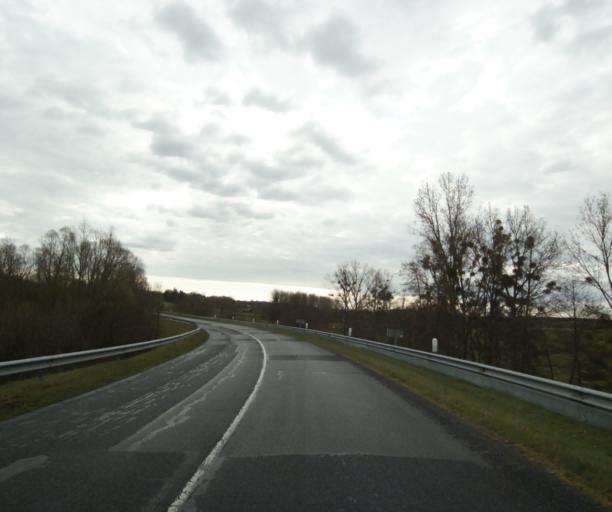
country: FR
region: Auvergne
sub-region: Departement de l'Allier
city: Toulon-sur-Allier
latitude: 46.4982
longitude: 3.3808
